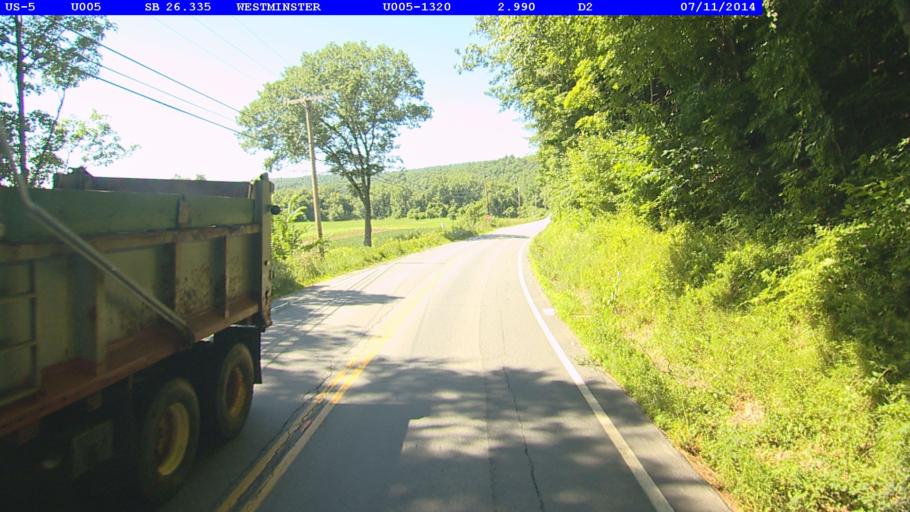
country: US
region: Vermont
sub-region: Windham County
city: Bellows Falls
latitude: 43.0609
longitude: -72.4651
